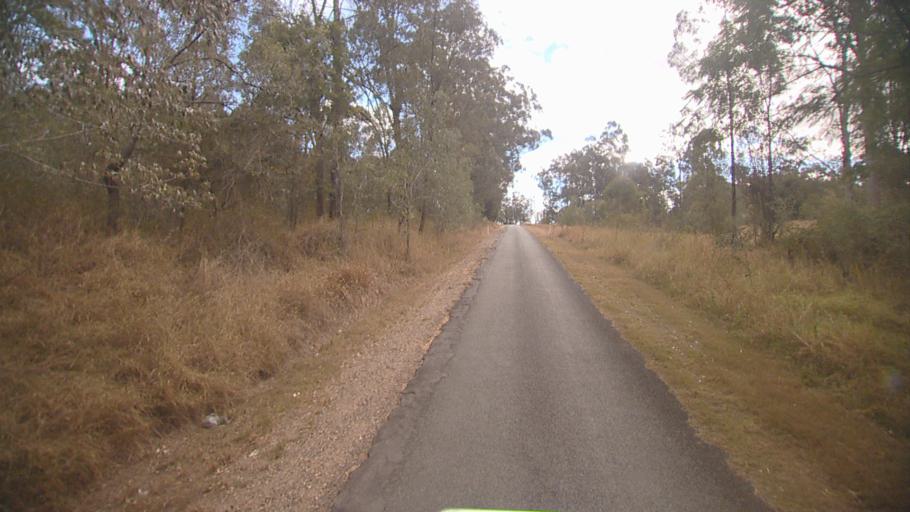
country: AU
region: Queensland
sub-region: Logan
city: Cedar Vale
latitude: -27.8792
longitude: 153.0296
